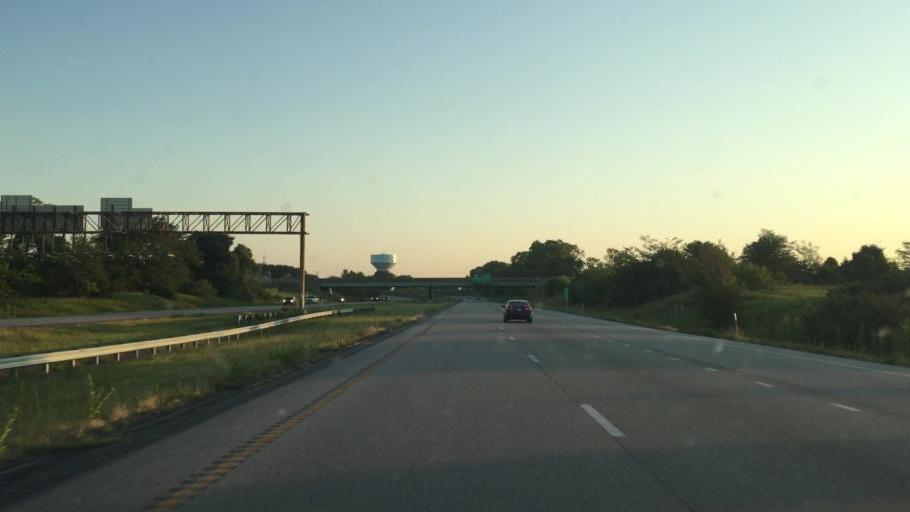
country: US
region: Missouri
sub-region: Clay County
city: Pleasant Valley
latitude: 39.3004
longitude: -94.5100
